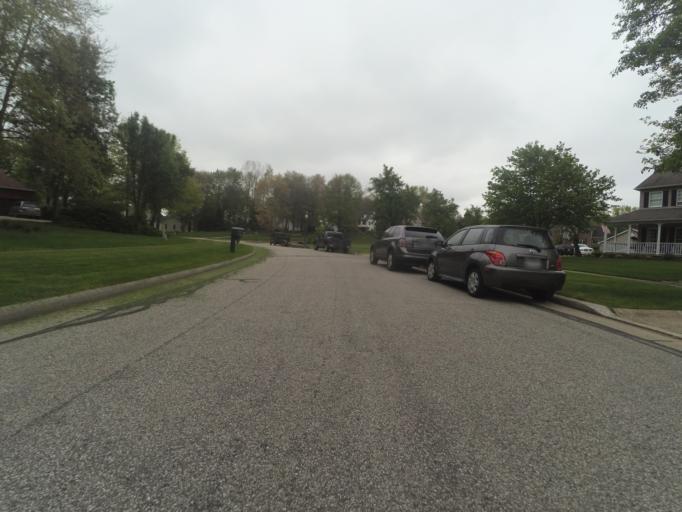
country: US
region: Ohio
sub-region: Portage County
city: Kent
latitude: 41.1704
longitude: -81.3475
